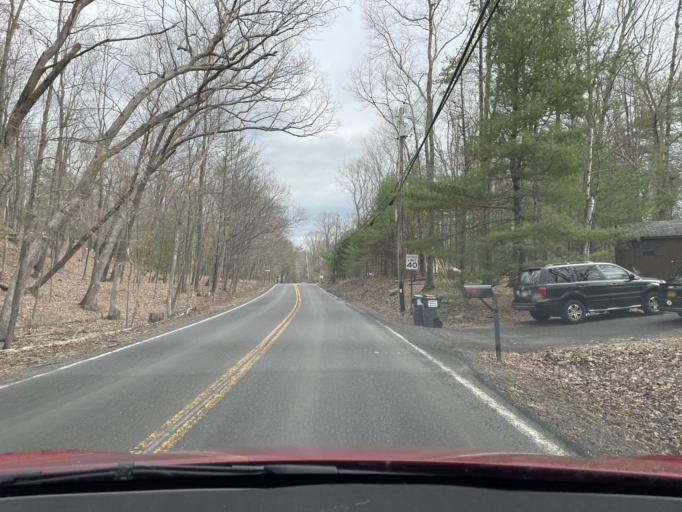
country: US
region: New York
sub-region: Ulster County
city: Woodstock
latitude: 42.0494
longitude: -74.1113
